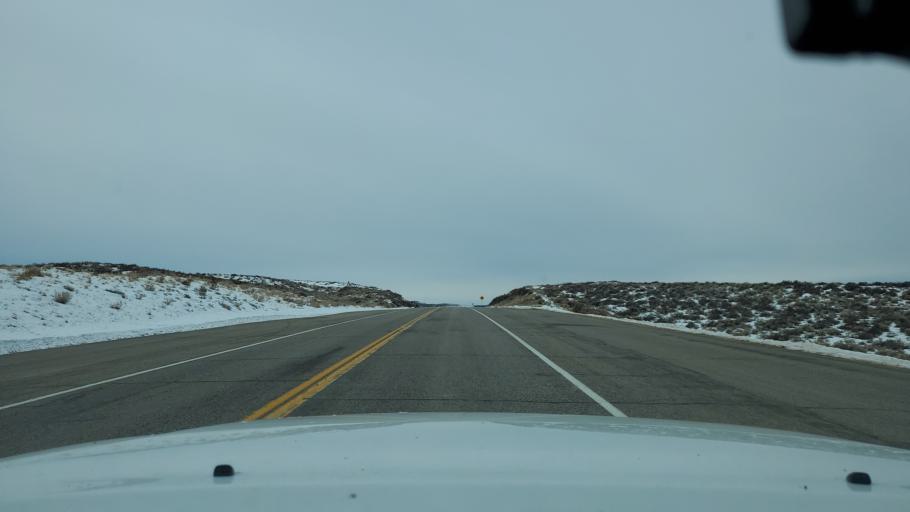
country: US
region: Colorado
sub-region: Rio Blanco County
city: Meeker
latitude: 40.4626
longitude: -108.2452
